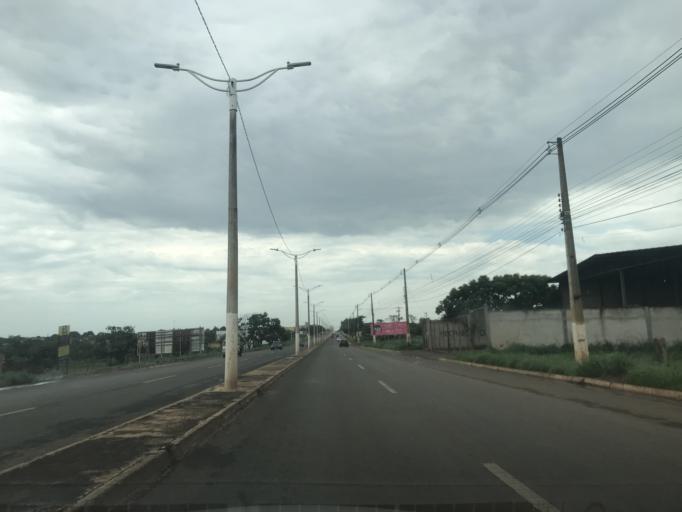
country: BR
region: Goias
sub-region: Luziania
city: Luziania
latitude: -16.2187
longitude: -47.9333
